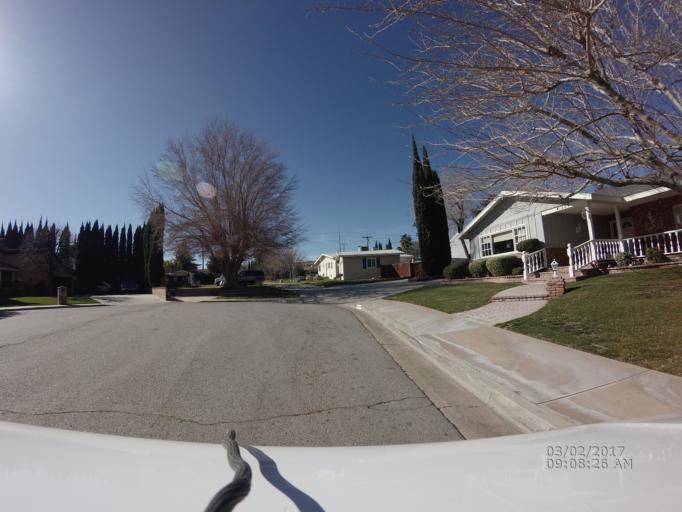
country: US
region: California
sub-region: Los Angeles County
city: Quartz Hill
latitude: 34.6318
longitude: -118.2146
